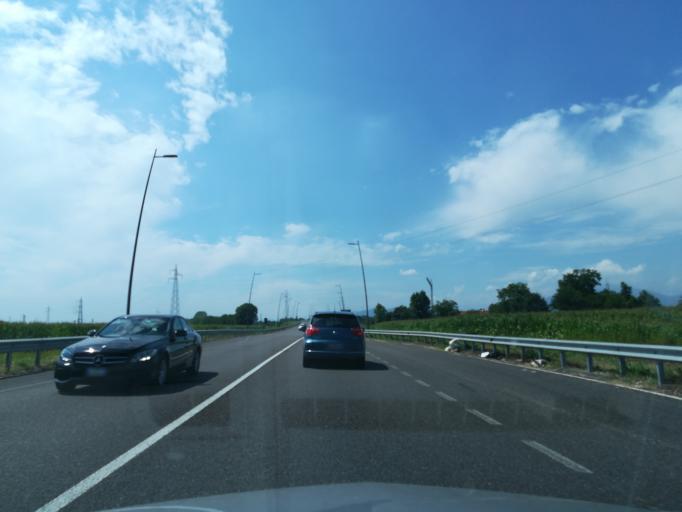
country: IT
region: Lombardy
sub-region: Provincia di Bergamo
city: Stezzano
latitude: 45.6350
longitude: 9.6512
